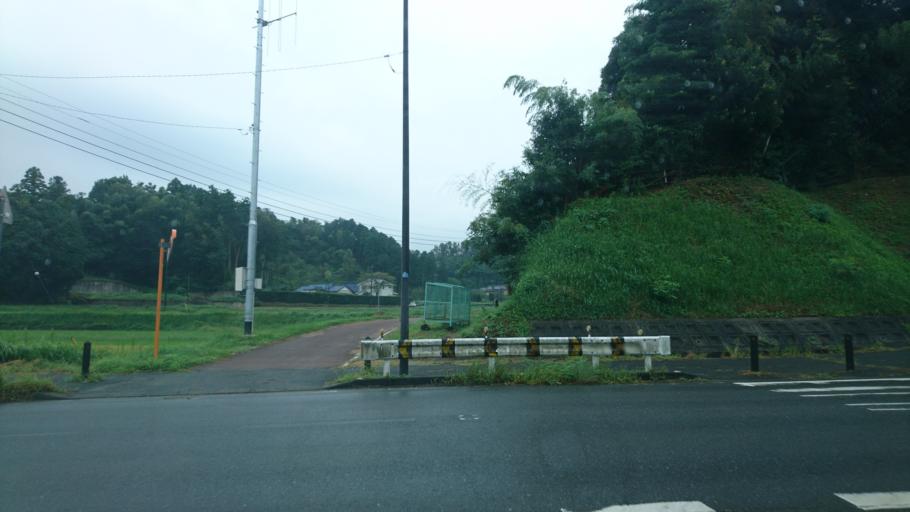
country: JP
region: Chiba
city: Kimitsu
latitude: 35.3052
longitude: 139.9369
